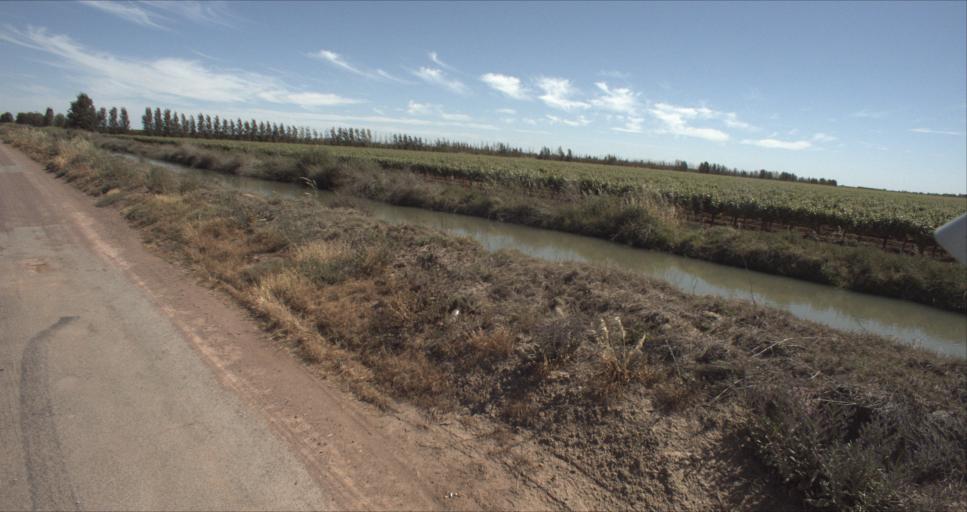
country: AU
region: New South Wales
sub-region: Leeton
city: Leeton
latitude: -34.5545
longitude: 146.3776
